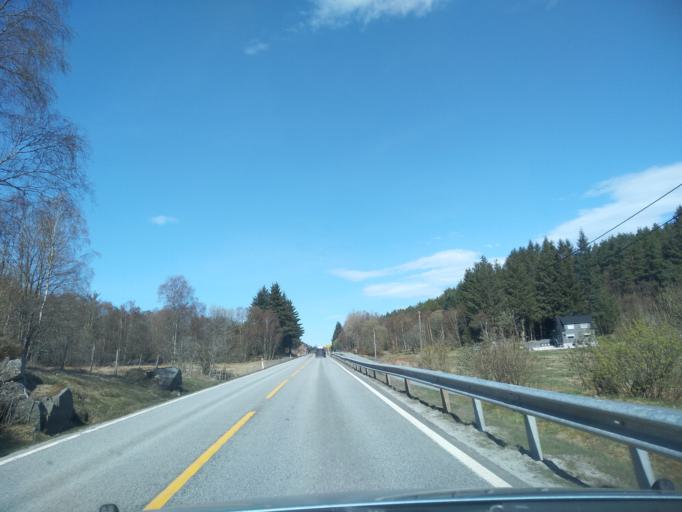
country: NO
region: Rogaland
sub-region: Tysvaer
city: Tysvaer
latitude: 59.3250
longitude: 5.4458
